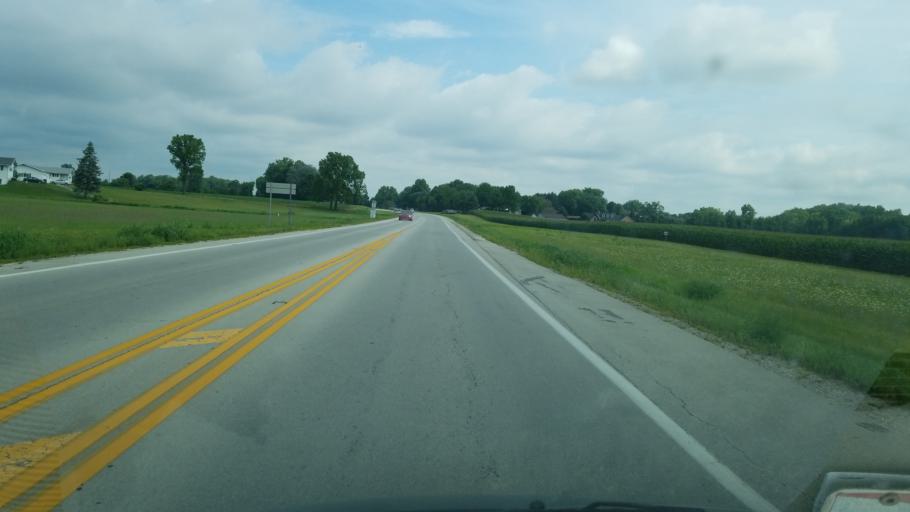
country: US
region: Ohio
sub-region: Sandusky County
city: Ballville
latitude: 41.2932
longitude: -83.1701
